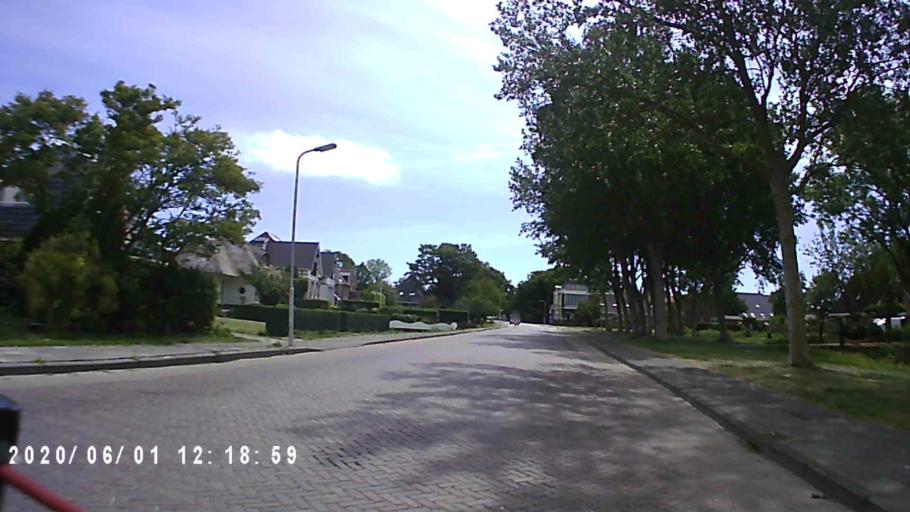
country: NL
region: Friesland
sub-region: Gemeente Harlingen
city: Harlingen
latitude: 53.1314
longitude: 5.4734
